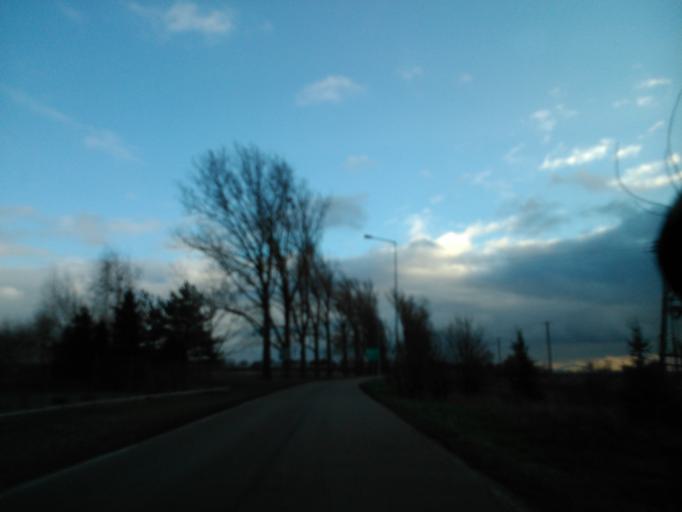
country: PL
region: Masovian Voivodeship
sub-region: Powiat warszawski zachodni
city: Blonie
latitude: 52.2121
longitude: 20.6538
